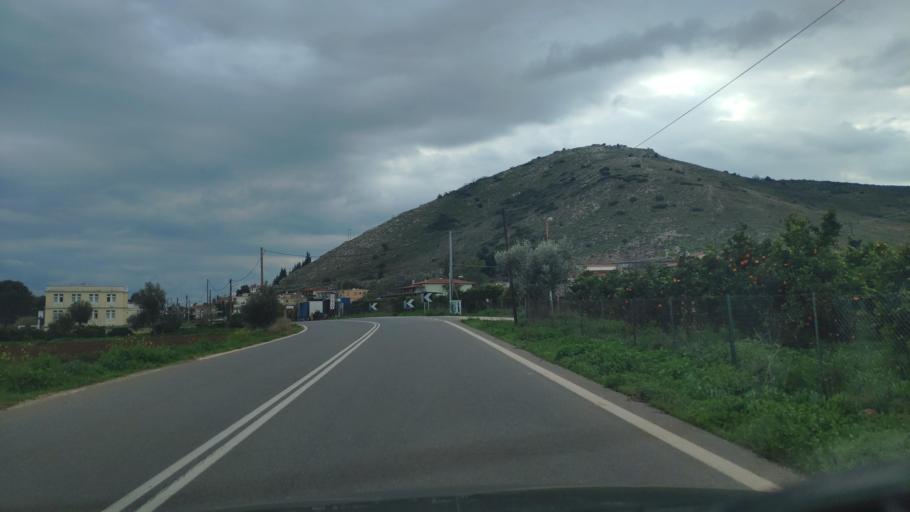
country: GR
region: Peloponnese
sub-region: Nomos Argolidos
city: Nea Kios
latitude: 37.5612
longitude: 22.7096
